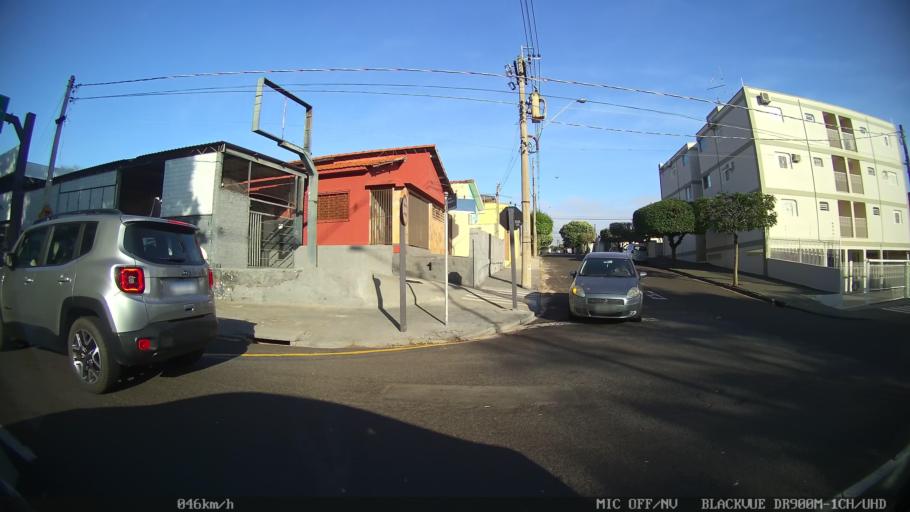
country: BR
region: Sao Paulo
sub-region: Sao Jose Do Rio Preto
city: Sao Jose do Rio Preto
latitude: -20.8157
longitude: -49.3667
